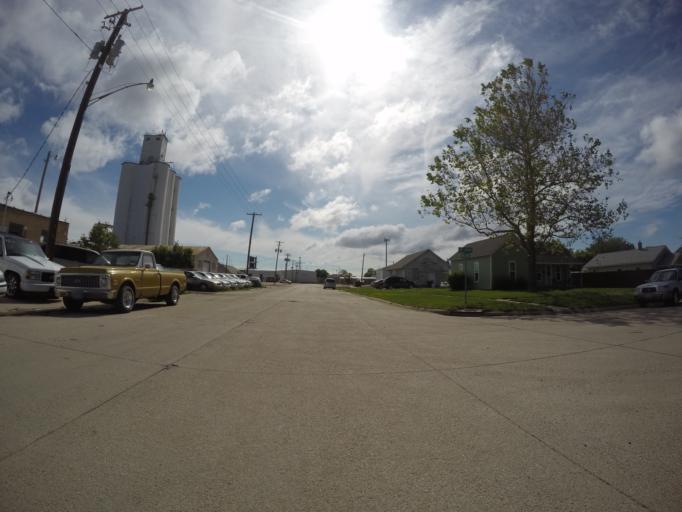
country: US
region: Nebraska
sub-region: Buffalo County
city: Kearney
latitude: 40.6935
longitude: -99.0874
